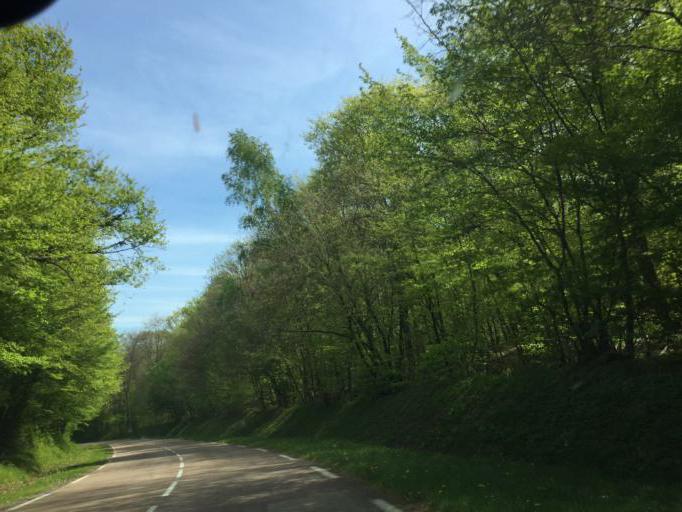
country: FR
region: Bourgogne
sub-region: Departement de la Nievre
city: Clamecy
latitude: 47.4542
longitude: 3.7092
